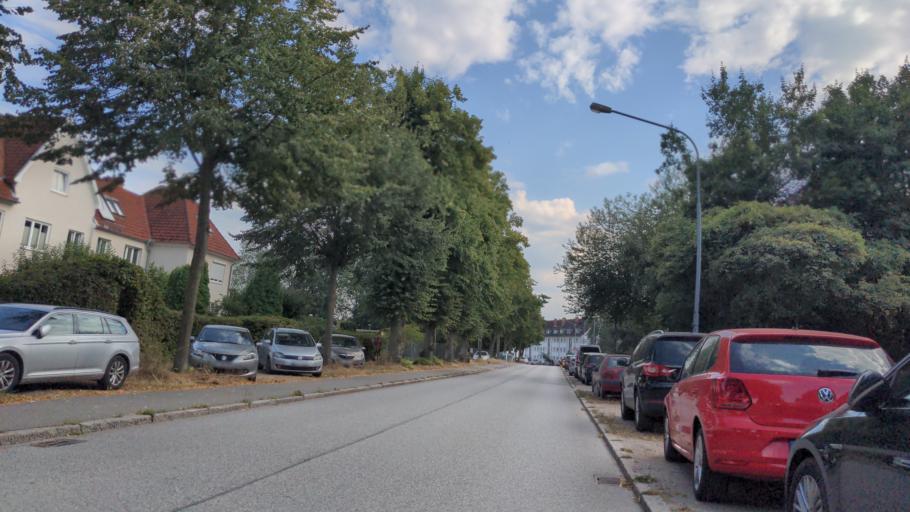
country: DE
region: Schleswig-Holstein
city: Luebeck
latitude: 53.8702
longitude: 10.7206
